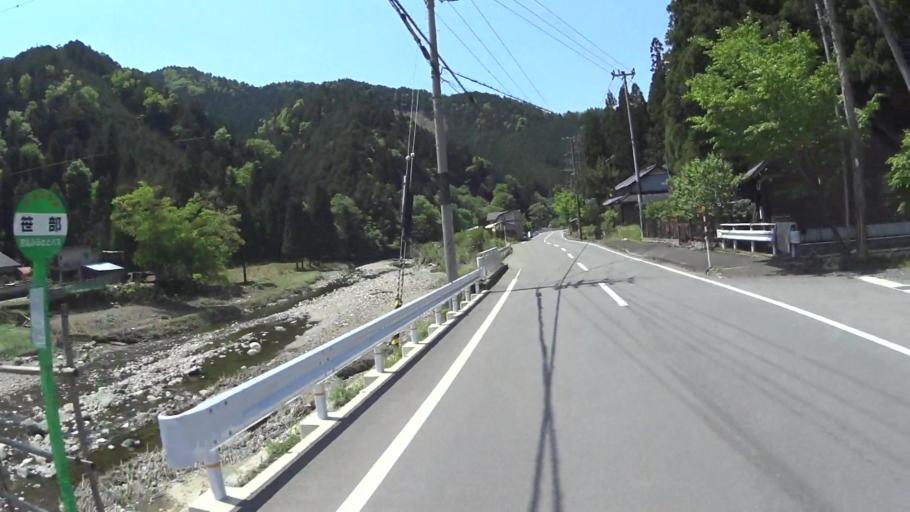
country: JP
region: Kyoto
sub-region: Kyoto-shi
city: Kamigyo-ku
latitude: 35.2047
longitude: 135.7279
